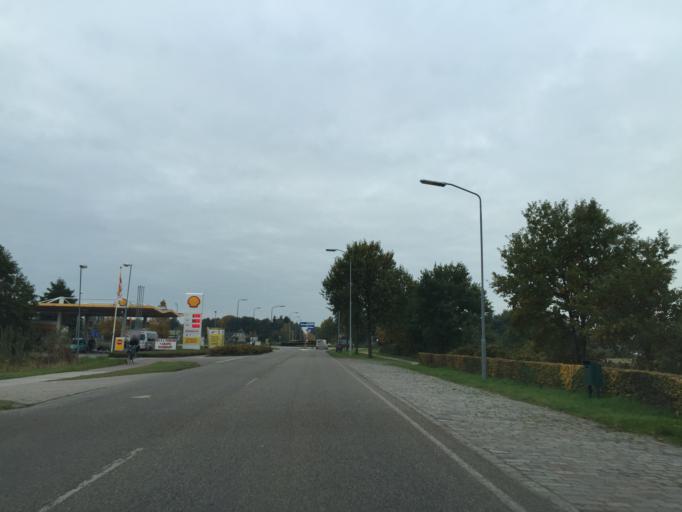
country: NL
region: North Brabant
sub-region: Gemeente Waalwijk
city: Waalwijk
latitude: 51.6667
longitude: 5.0533
